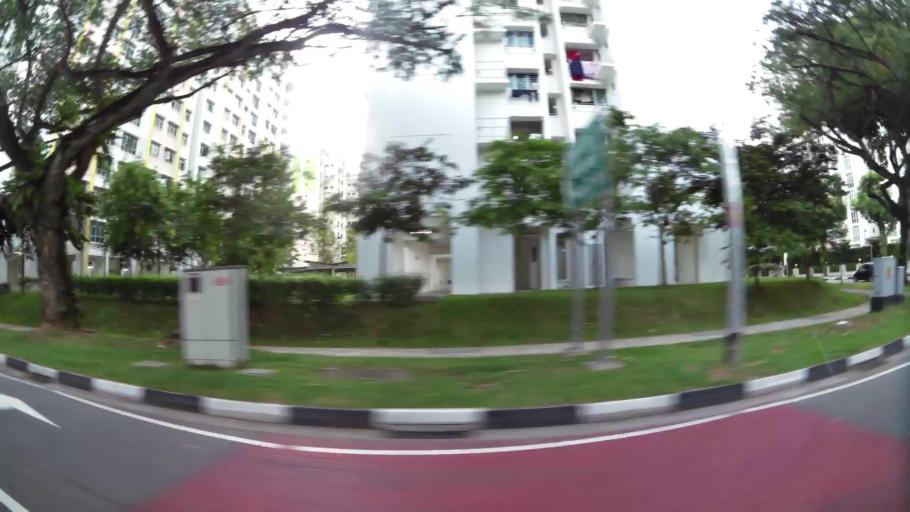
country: MY
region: Johor
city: Kampung Pasir Gudang Baru
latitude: 1.4232
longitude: 103.8495
